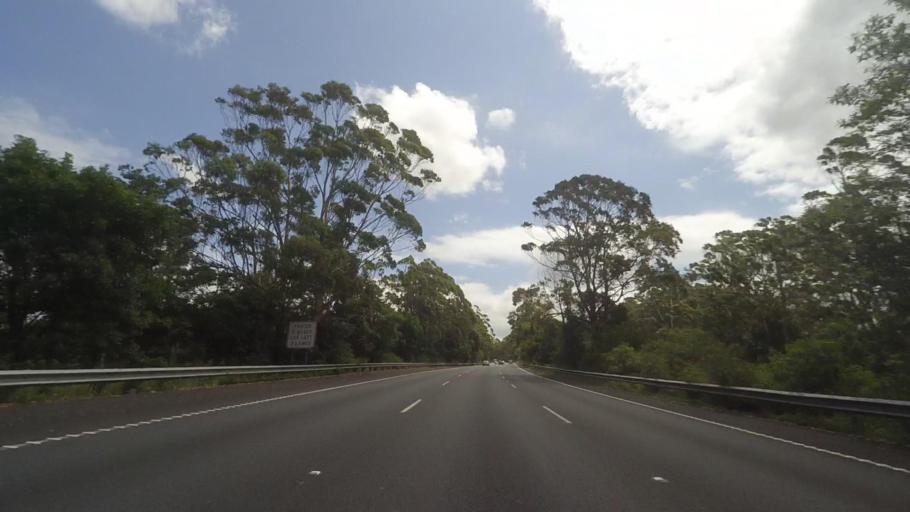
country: AU
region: New South Wales
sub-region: Gosford Shire
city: Lisarow
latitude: -33.3515
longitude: 151.3618
